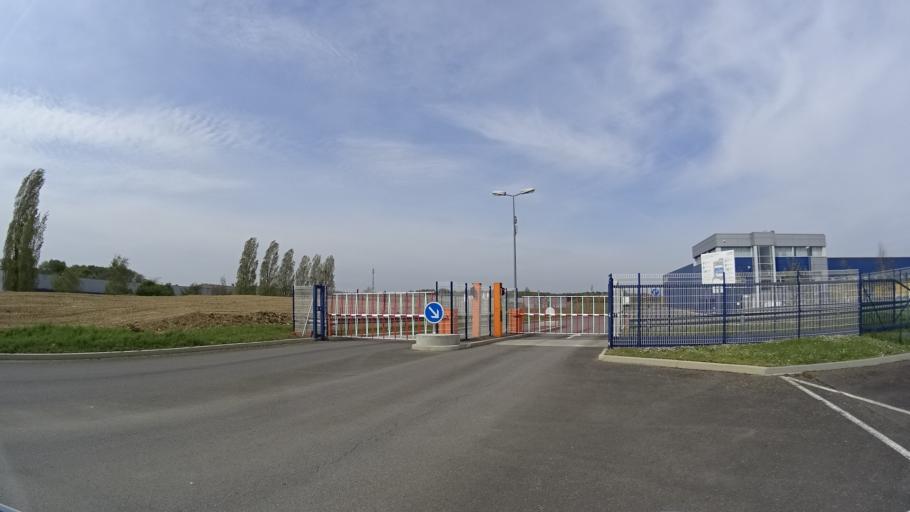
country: FR
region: Brittany
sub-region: Departement d'Ille-et-Vilaine
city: Bruz
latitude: 48.0361
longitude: -1.7343
